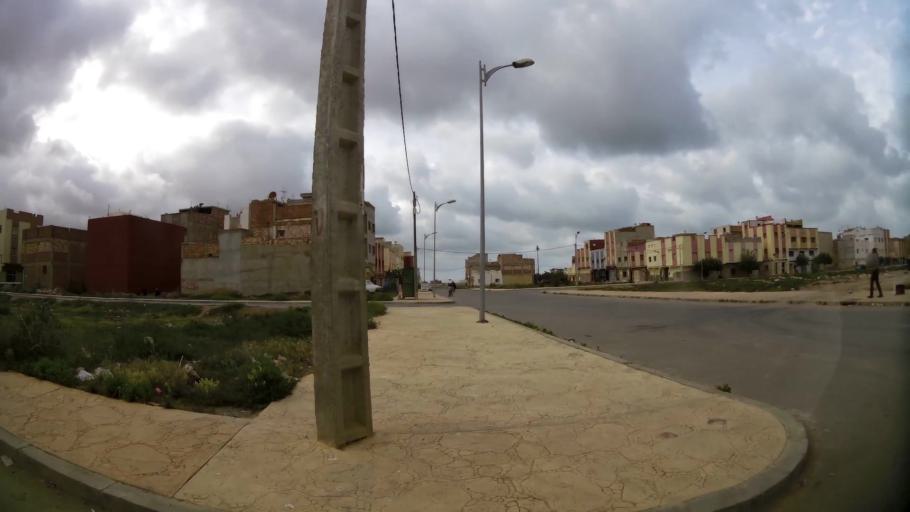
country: MA
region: Oriental
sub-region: Nador
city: Nador
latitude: 35.1577
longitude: -2.9112
